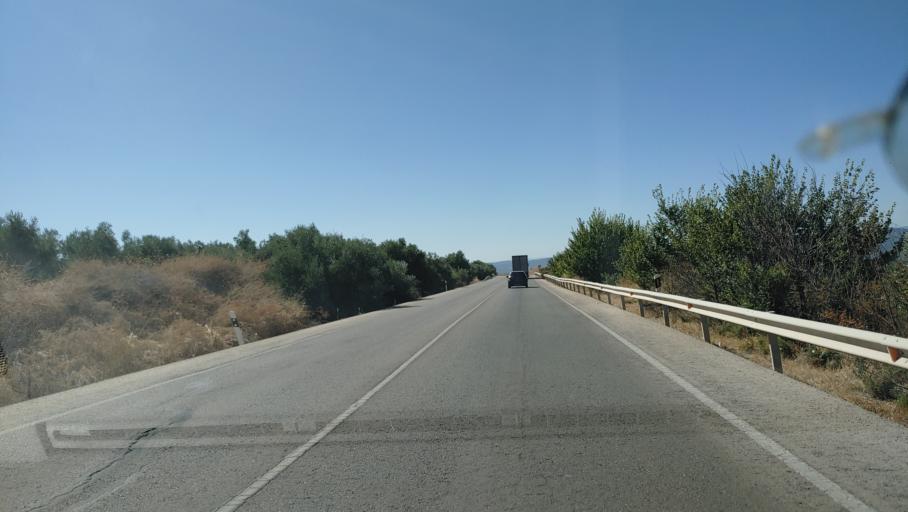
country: ES
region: Andalusia
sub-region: Provincia de Jaen
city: Villacarrillo
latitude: 38.1037
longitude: -3.1112
